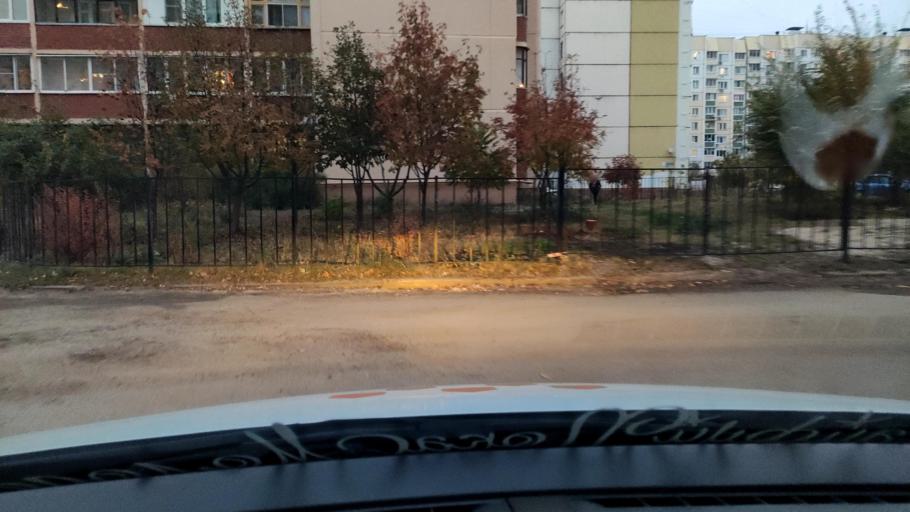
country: RU
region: Voronezj
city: Podgornoye
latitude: 51.7212
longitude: 39.1666
